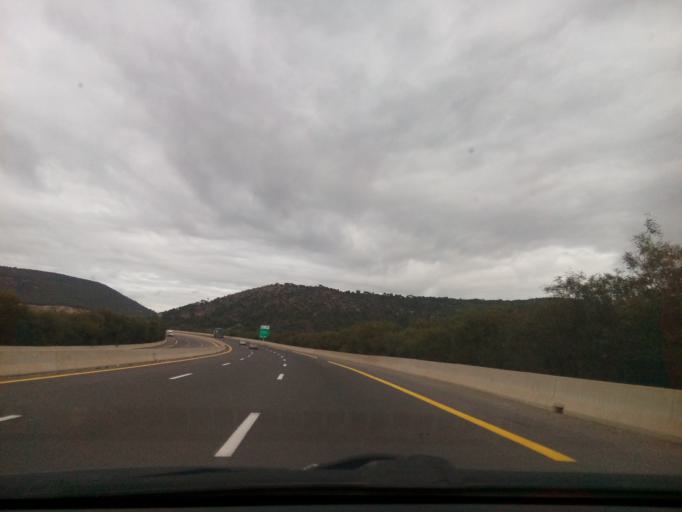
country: DZ
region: Sidi Bel Abbes
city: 'Ain el Berd
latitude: 35.3673
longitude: -0.5012
